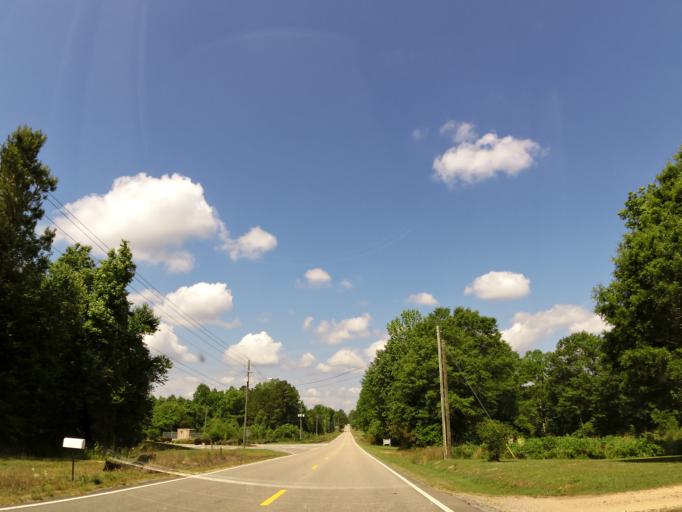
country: US
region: Alabama
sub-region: Marion County
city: Winfield
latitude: 34.0107
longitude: -87.8416
